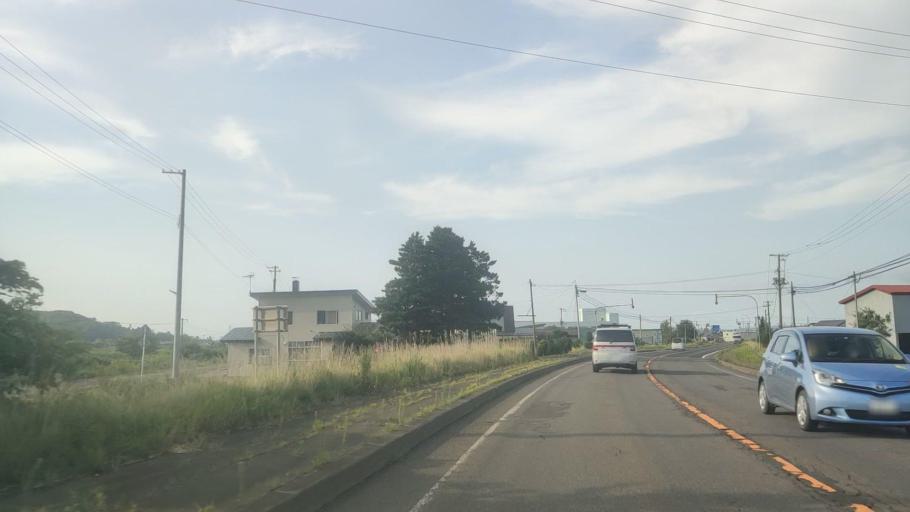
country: JP
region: Hokkaido
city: Iwamizawa
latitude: 43.0029
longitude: 141.7885
